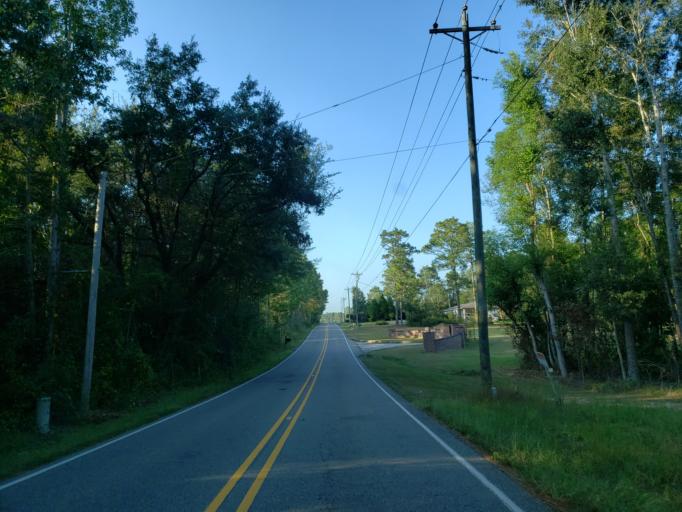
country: US
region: Mississippi
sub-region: Lamar County
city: West Hattiesburg
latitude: 31.3116
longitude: -89.4440
